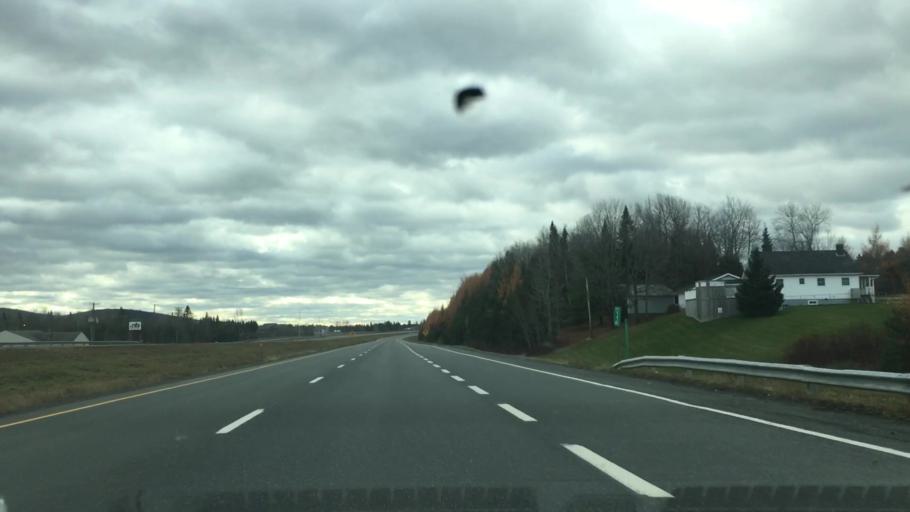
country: US
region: Maine
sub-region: Aroostook County
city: Fort Fairfield
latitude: 46.7476
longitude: -67.7147
